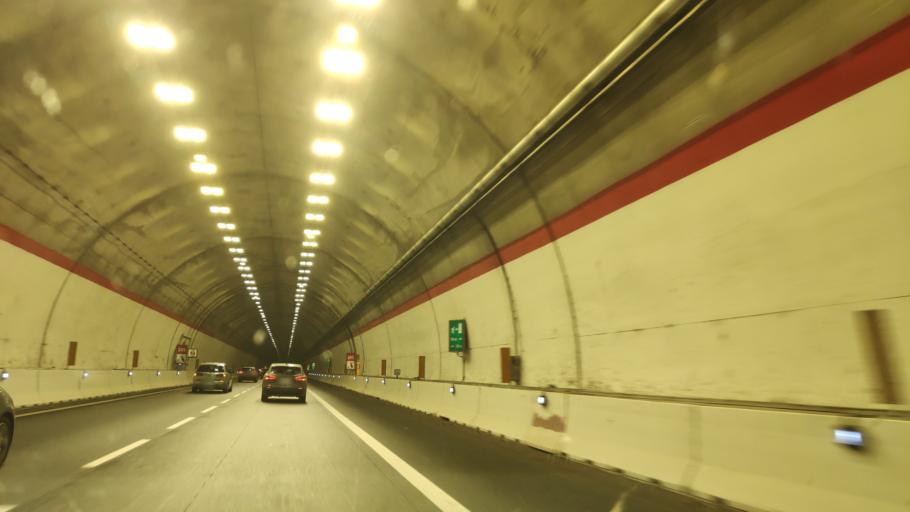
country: IT
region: Campania
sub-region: Provincia di Salerno
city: Sicignano degli Alburni
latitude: 40.5779
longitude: 15.3450
